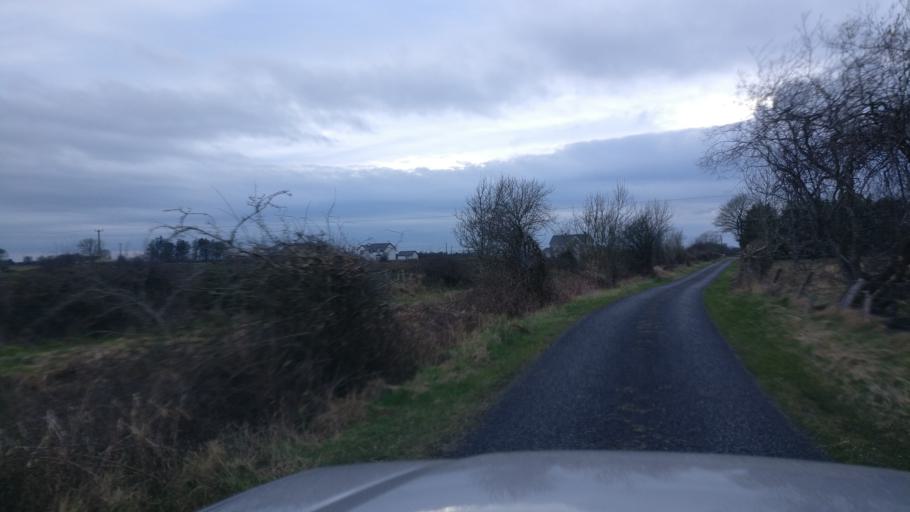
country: IE
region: Connaught
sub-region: County Galway
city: Loughrea
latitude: 53.2579
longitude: -8.5047
